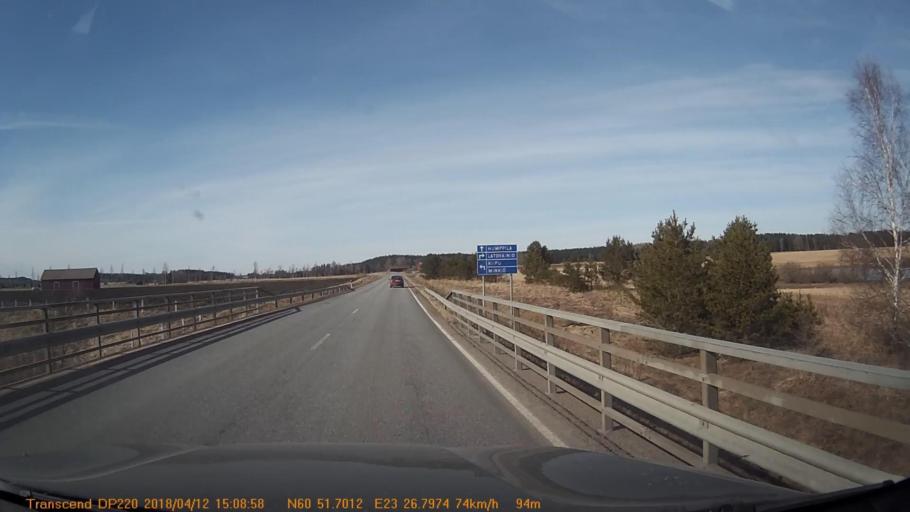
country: FI
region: Haeme
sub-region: Forssa
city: Jokioinen
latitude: 60.8617
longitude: 23.4466
